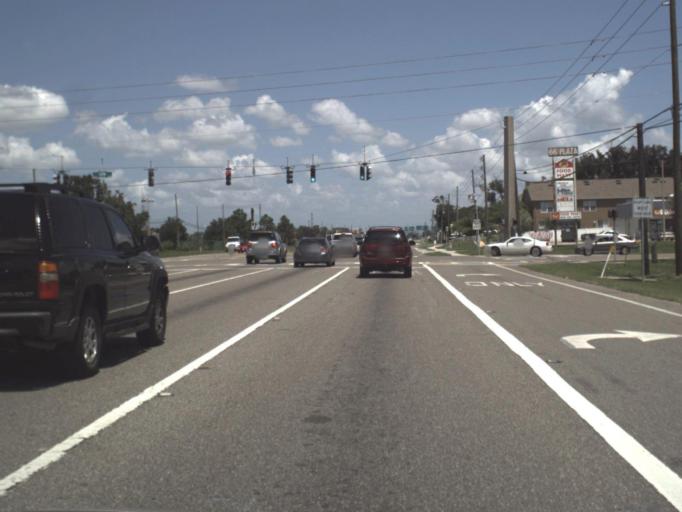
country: US
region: Florida
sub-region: Pinellas County
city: South Highpoint
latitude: 27.8859
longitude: -82.7290
